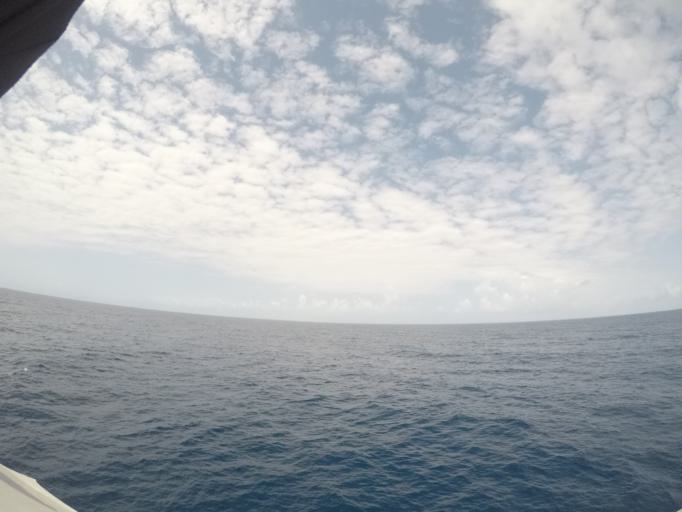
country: TZ
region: Zanzibar North
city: Nungwi
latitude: -5.5827
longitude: 39.3574
